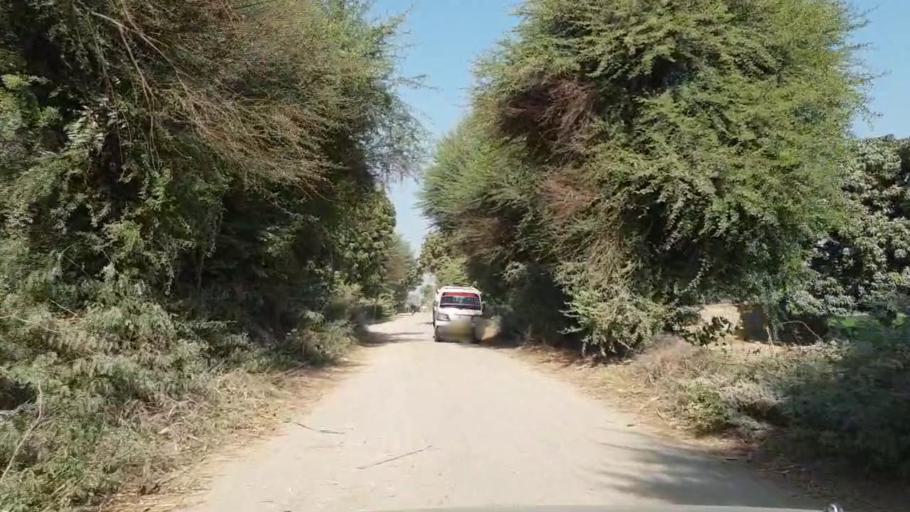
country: PK
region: Sindh
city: Matiari
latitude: 25.6056
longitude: 68.5981
